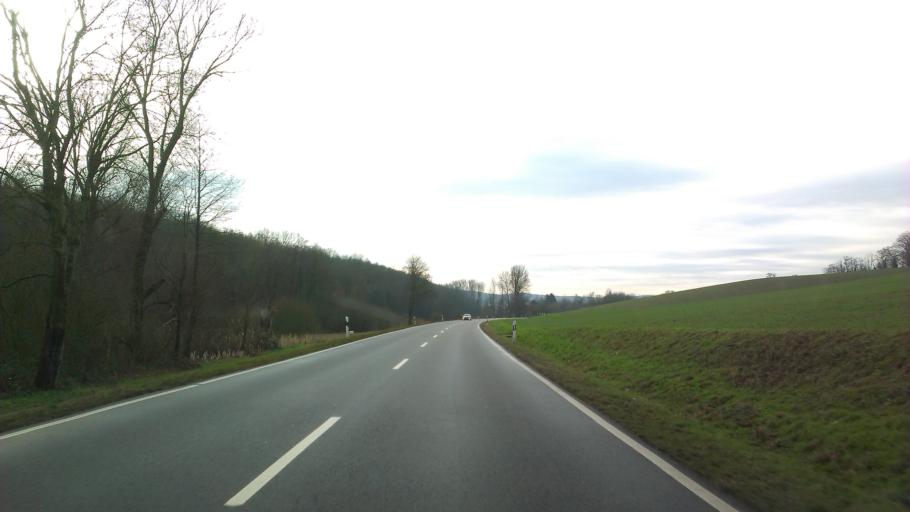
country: DE
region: Baden-Wuerttemberg
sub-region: Karlsruhe Region
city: Horrenberg
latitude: 49.2982
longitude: 8.7797
